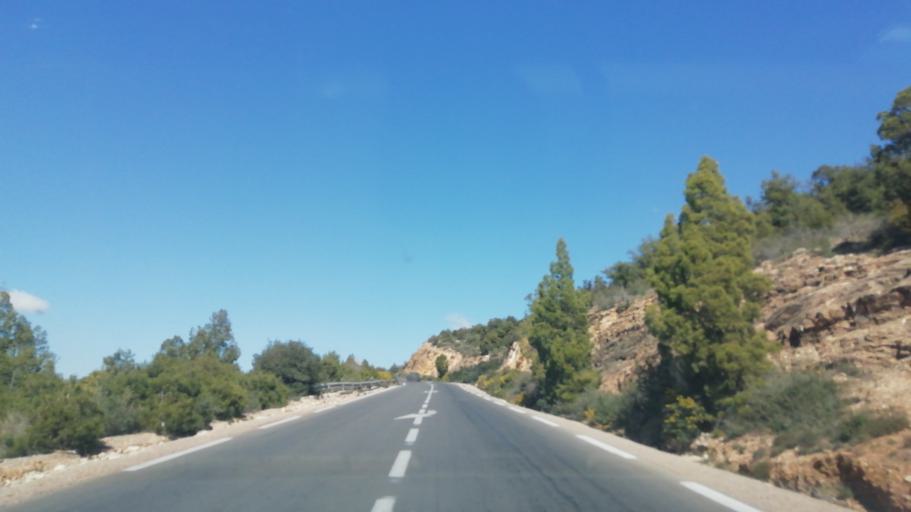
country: DZ
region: Mascara
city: Mascara
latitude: 35.4872
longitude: 0.1470
